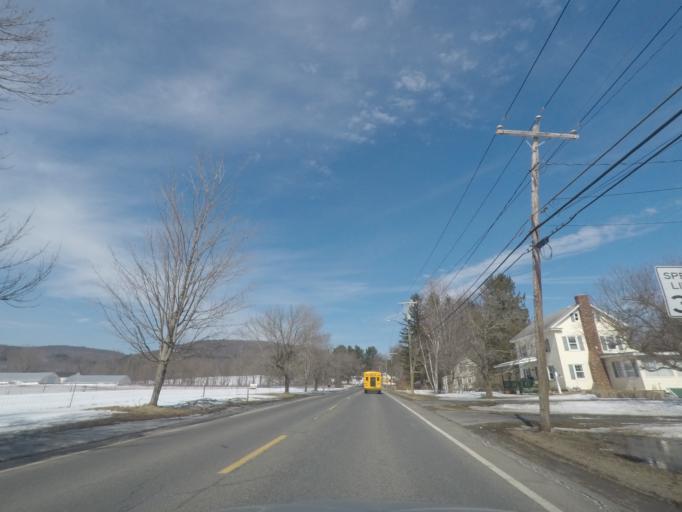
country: US
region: Massachusetts
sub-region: Berkshire County
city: Richmond
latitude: 42.4295
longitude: -73.3329
